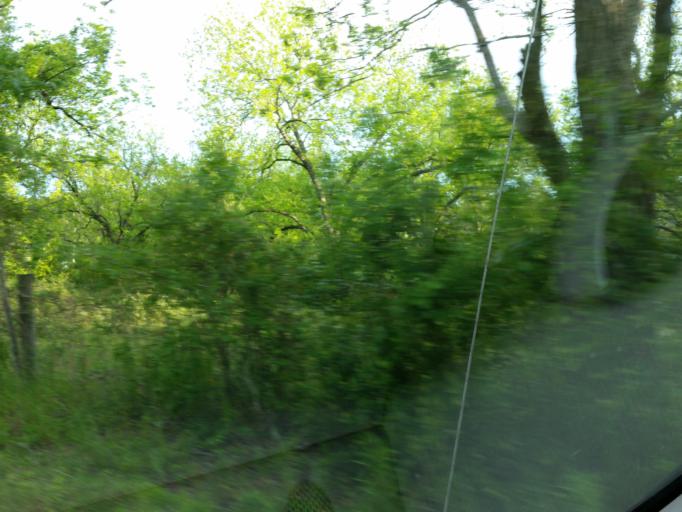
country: US
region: Georgia
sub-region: Turner County
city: Ashburn
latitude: 31.6929
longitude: -83.6412
